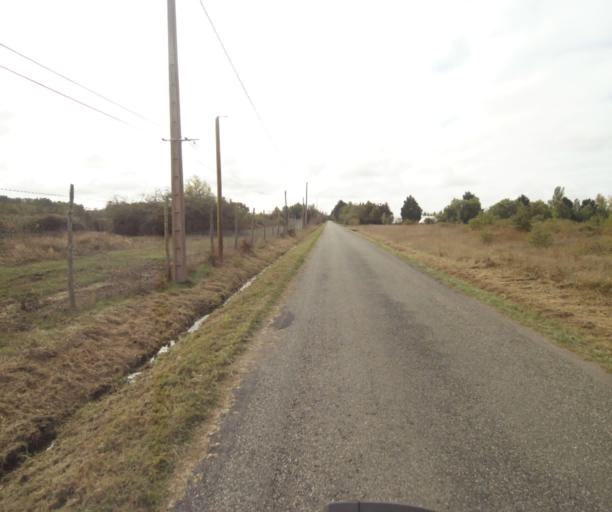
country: FR
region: Midi-Pyrenees
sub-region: Departement du Tarn-et-Garonne
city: Finhan
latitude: 43.9264
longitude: 1.2469
